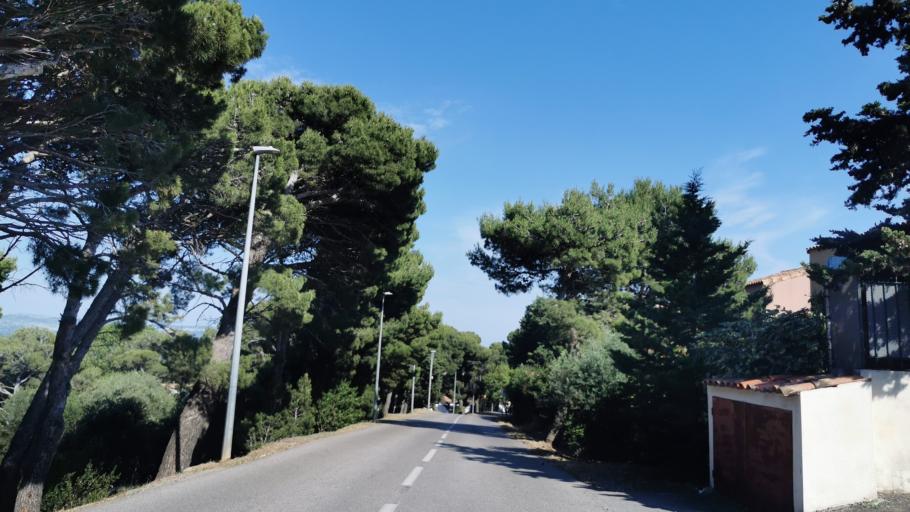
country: FR
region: Languedoc-Roussillon
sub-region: Departement de l'Aude
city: Peyriac-de-Mer
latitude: 43.1402
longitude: 2.9675
